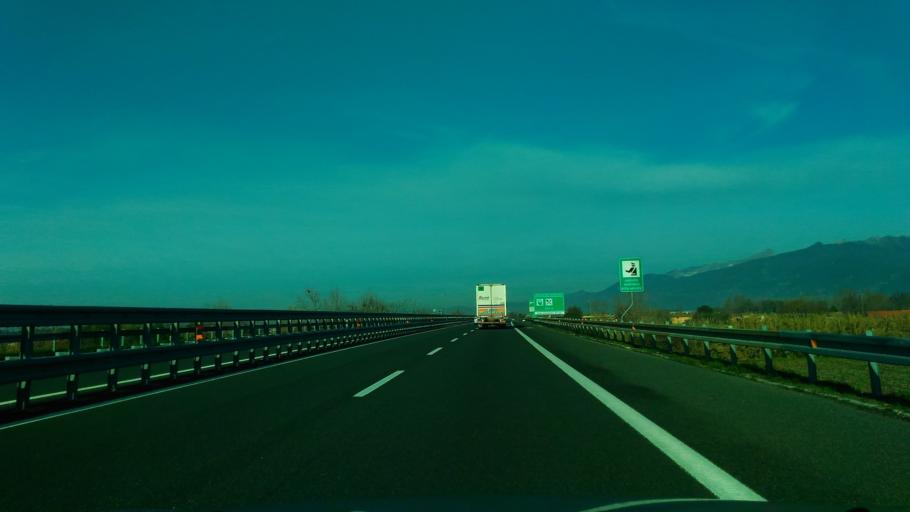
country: IT
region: Tuscany
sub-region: Provincia di Lucca
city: Pietrasanta
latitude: 43.9225
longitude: 10.2286
